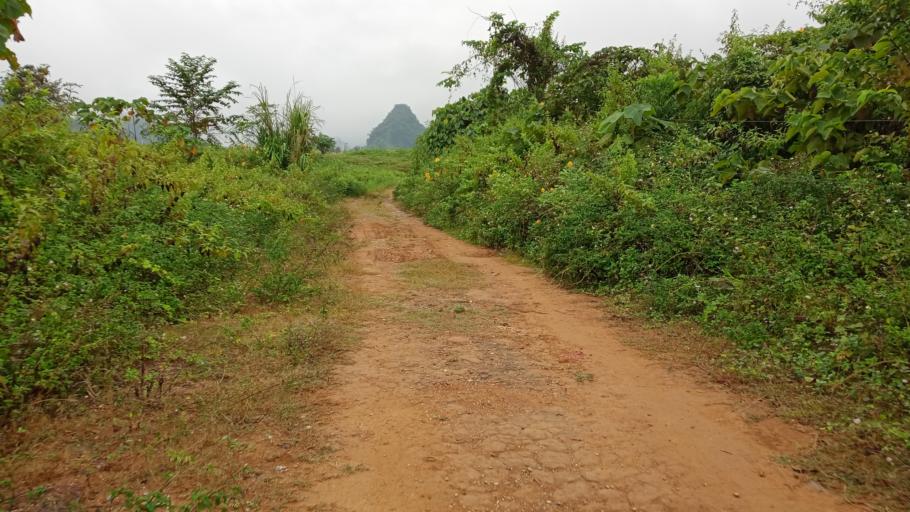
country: LA
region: Xiangkhoang
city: Phonsavan
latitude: 19.1032
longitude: 102.9282
